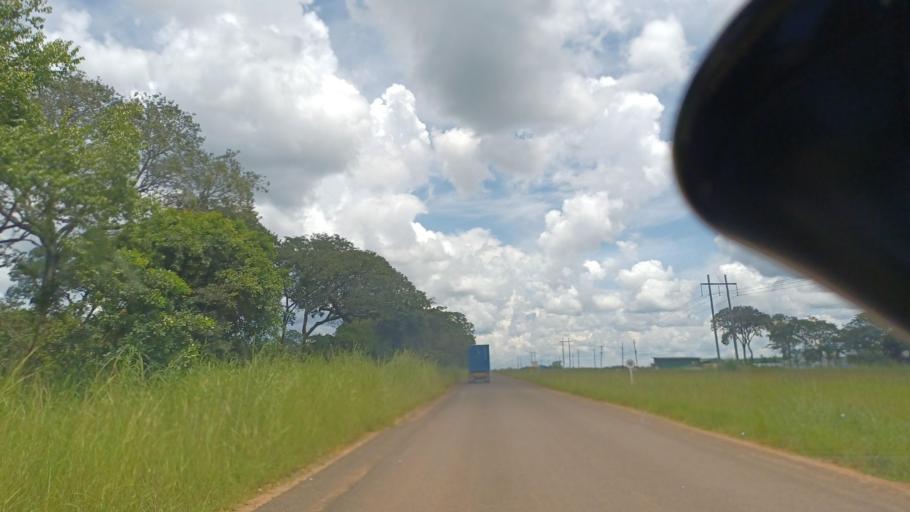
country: ZM
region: North-Western
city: Solwezi
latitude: -12.4364
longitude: 26.2103
